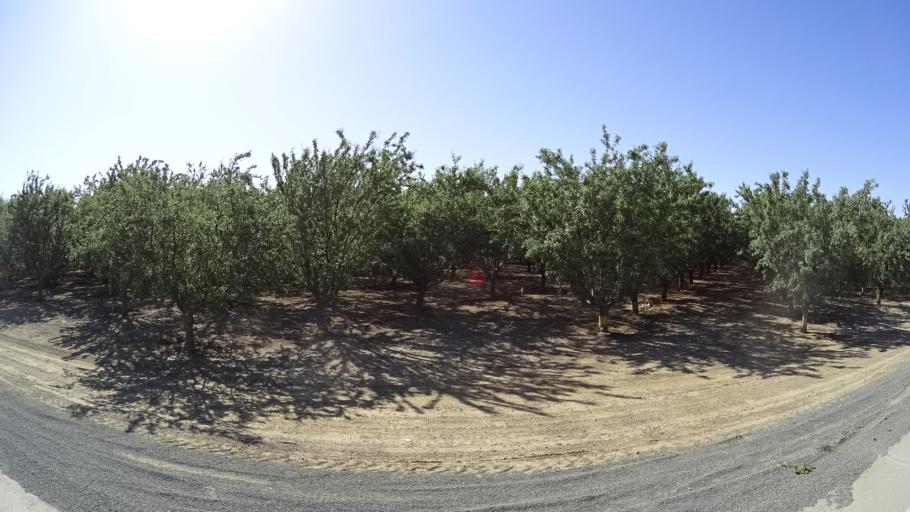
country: US
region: California
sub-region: Fresno County
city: Huron
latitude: 36.1555
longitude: -119.9887
